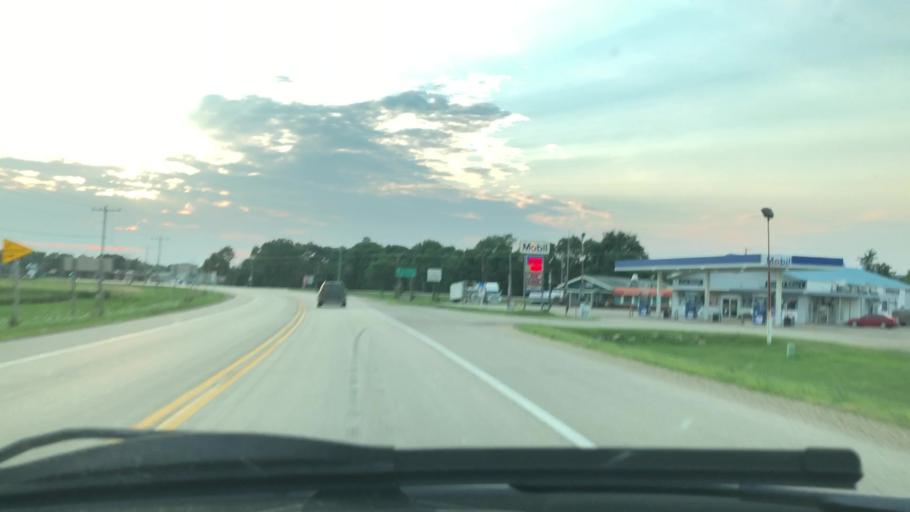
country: US
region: Wisconsin
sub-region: Sauk County
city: Spring Green
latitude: 43.1883
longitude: -90.0678
